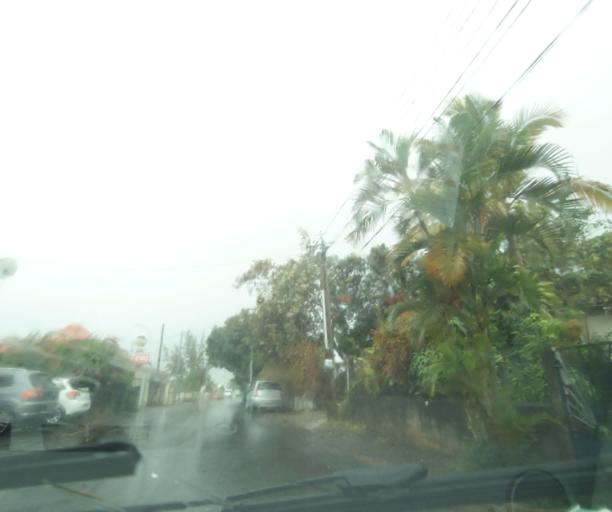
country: RE
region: Reunion
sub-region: Reunion
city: La Possession
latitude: -20.9821
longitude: 55.3270
